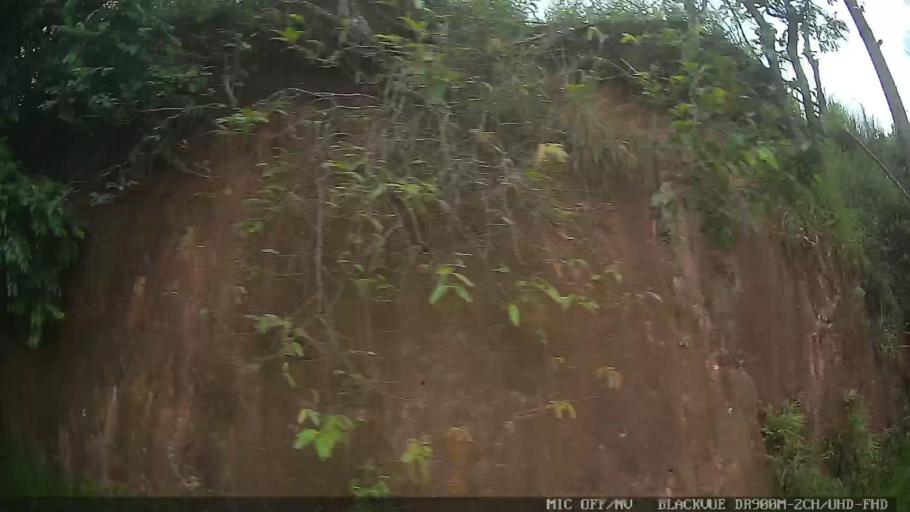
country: BR
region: Sao Paulo
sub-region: Aruja
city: Aruja
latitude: -23.4514
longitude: -46.2988
